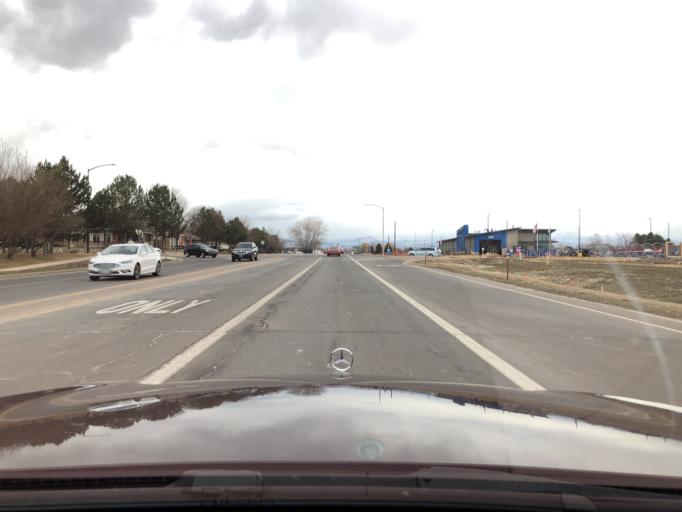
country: US
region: Colorado
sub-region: Boulder County
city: Louisville
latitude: 40.0147
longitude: -105.1268
